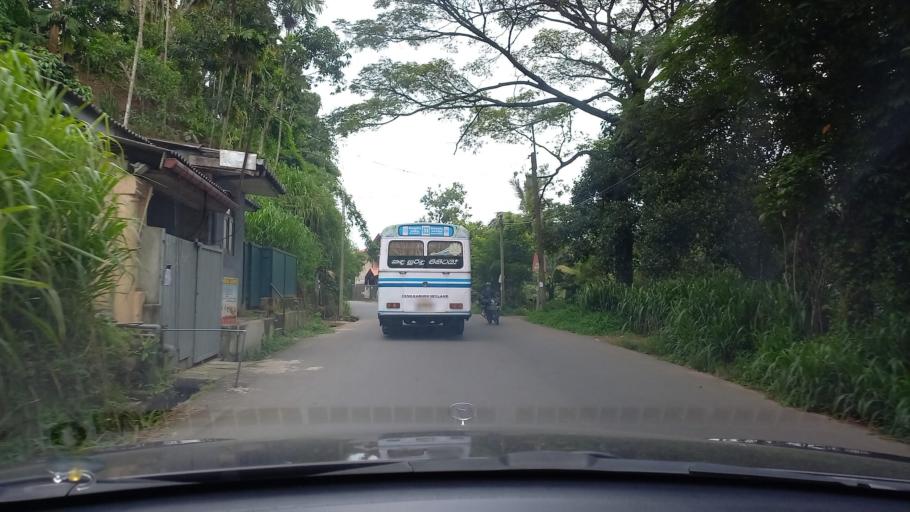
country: LK
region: Central
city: Kandy
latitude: 7.2412
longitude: 80.6003
